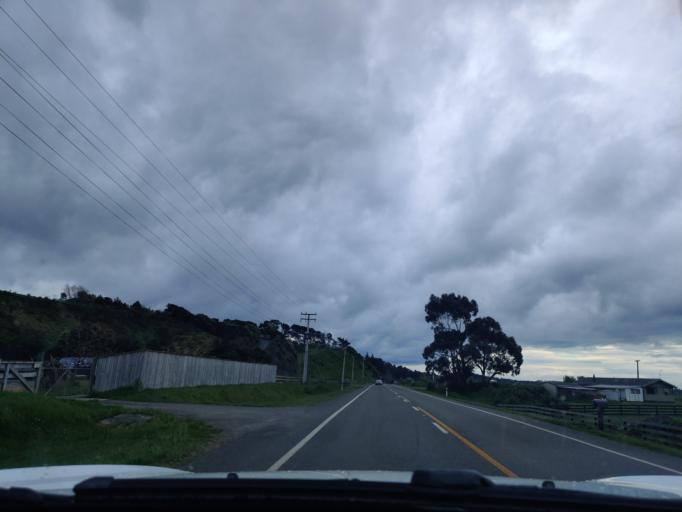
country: NZ
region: Manawatu-Wanganui
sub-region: Palmerston North City
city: Palmerston North
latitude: -40.3187
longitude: 175.7521
